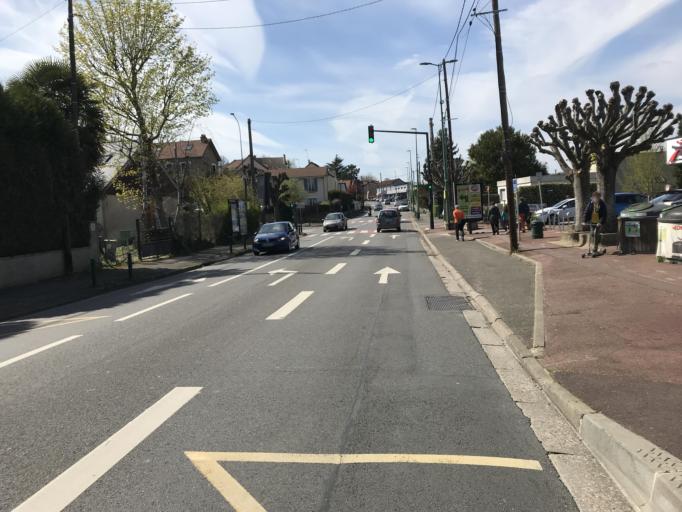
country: FR
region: Ile-de-France
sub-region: Departement de l'Essonne
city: Villebon-sur-Yvette
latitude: 48.7001
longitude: 2.2149
